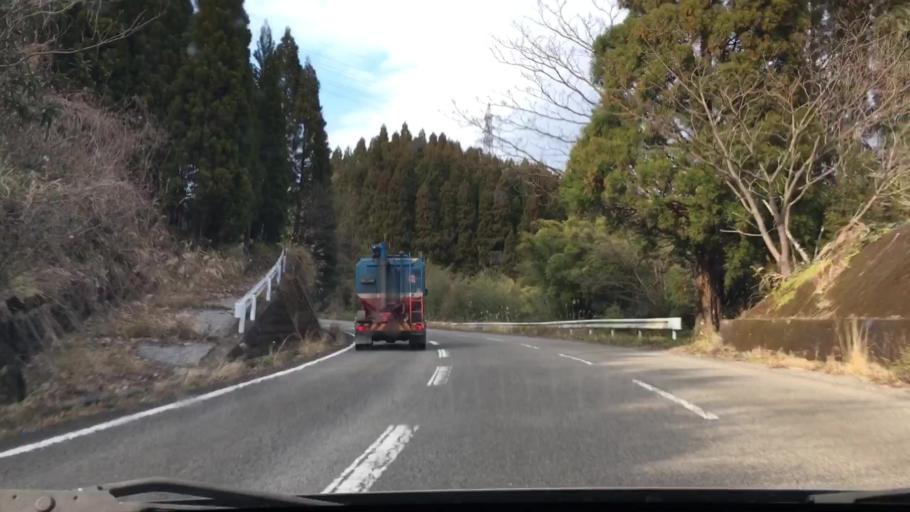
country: JP
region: Miyazaki
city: Nichinan
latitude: 31.6333
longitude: 131.3390
